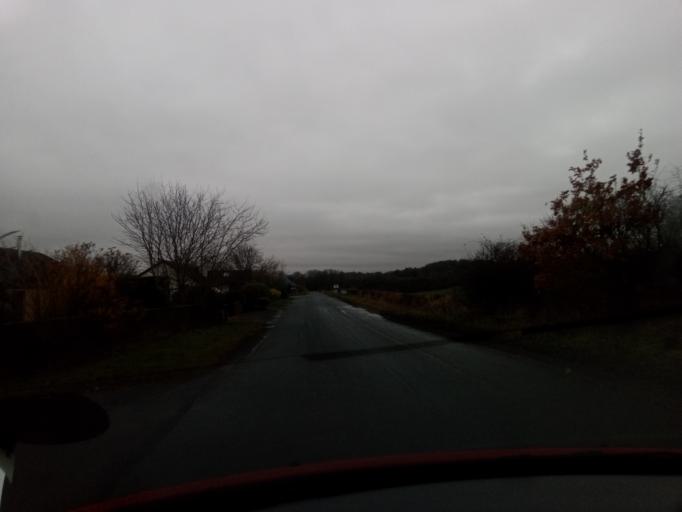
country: GB
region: Scotland
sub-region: The Scottish Borders
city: Saint Boswells
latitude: 55.5593
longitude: -2.6631
